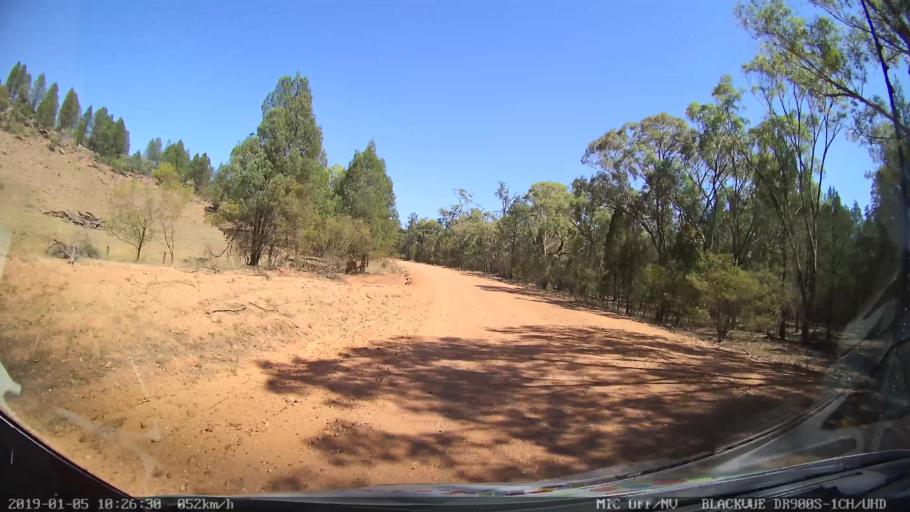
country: AU
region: New South Wales
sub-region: Gilgandra
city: Gilgandra
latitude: -31.5532
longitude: 148.9548
